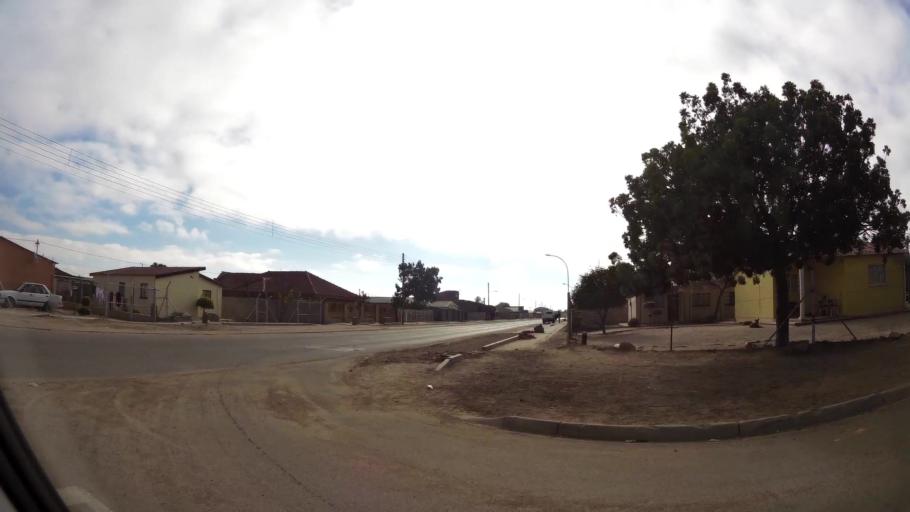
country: ZA
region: Limpopo
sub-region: Capricorn District Municipality
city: Polokwane
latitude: -23.8412
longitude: 29.3830
